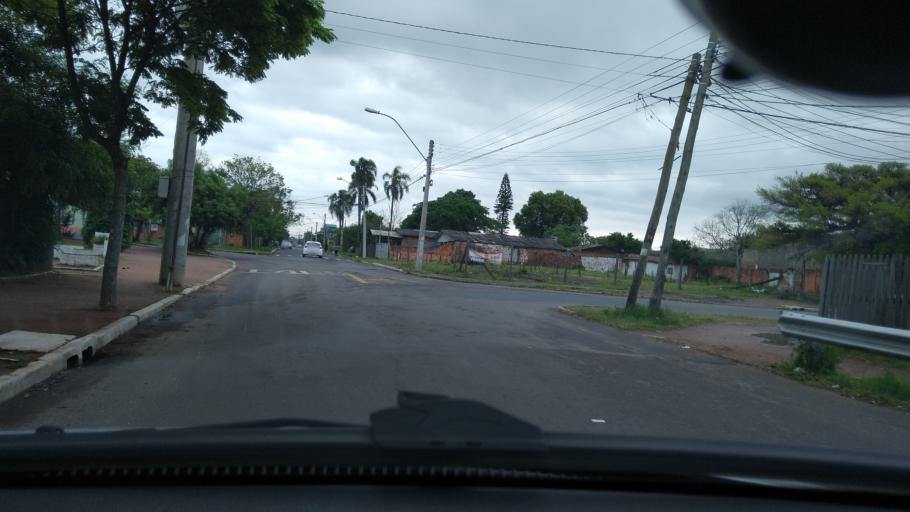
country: BR
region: Rio Grande do Sul
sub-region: Canoas
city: Canoas
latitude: -29.9017
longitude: -51.2056
